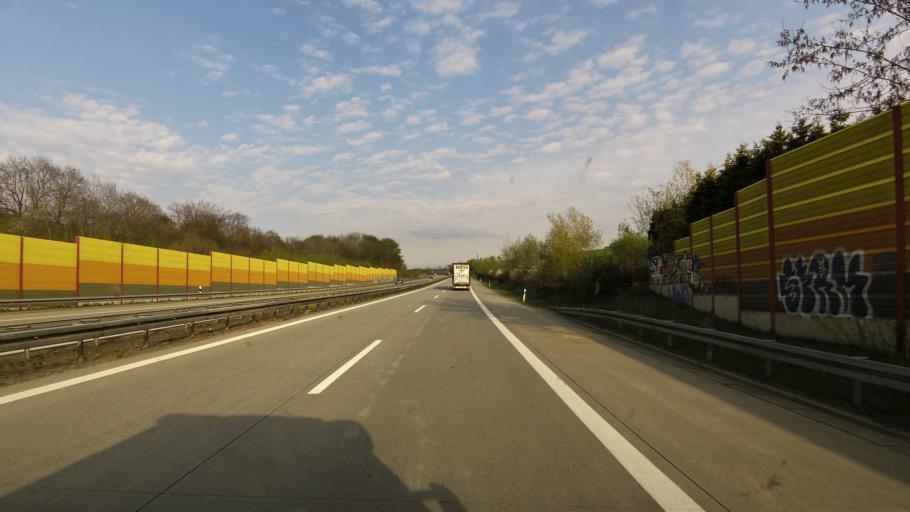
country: DE
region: Saxony
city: Hartenstein
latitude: 50.6907
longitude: 12.6738
